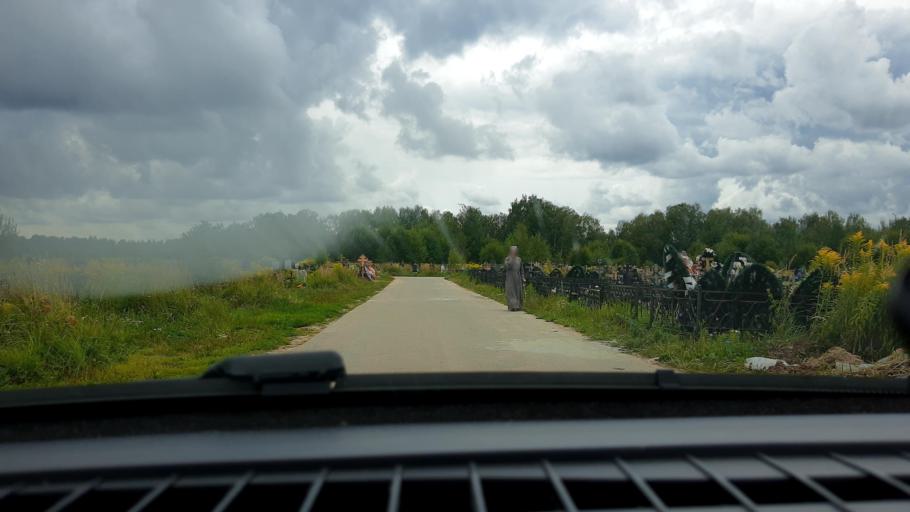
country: RU
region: Nizjnij Novgorod
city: Afonino
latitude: 56.2331
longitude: 44.0789
